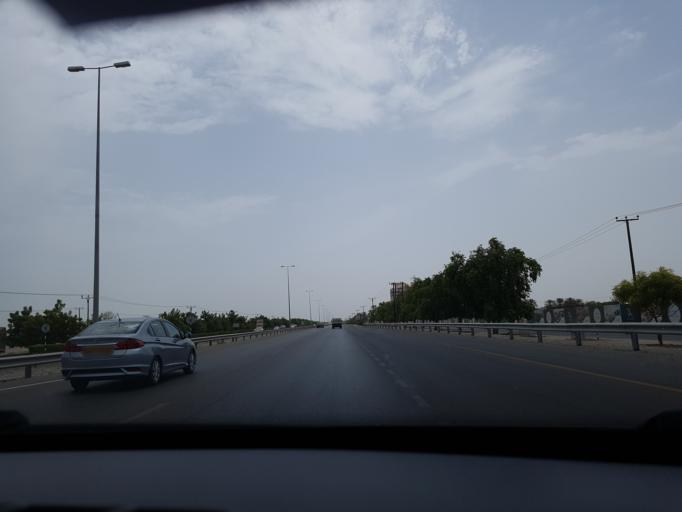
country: OM
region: Al Batinah
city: Barka'
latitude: 23.6627
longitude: 57.9052
